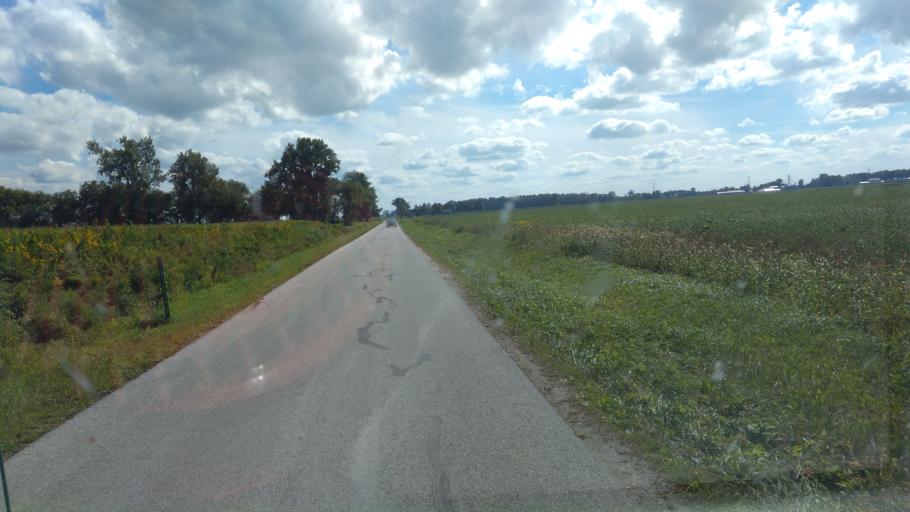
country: US
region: Ohio
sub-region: Ottawa County
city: Port Clinton
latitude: 41.4067
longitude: -82.8825
